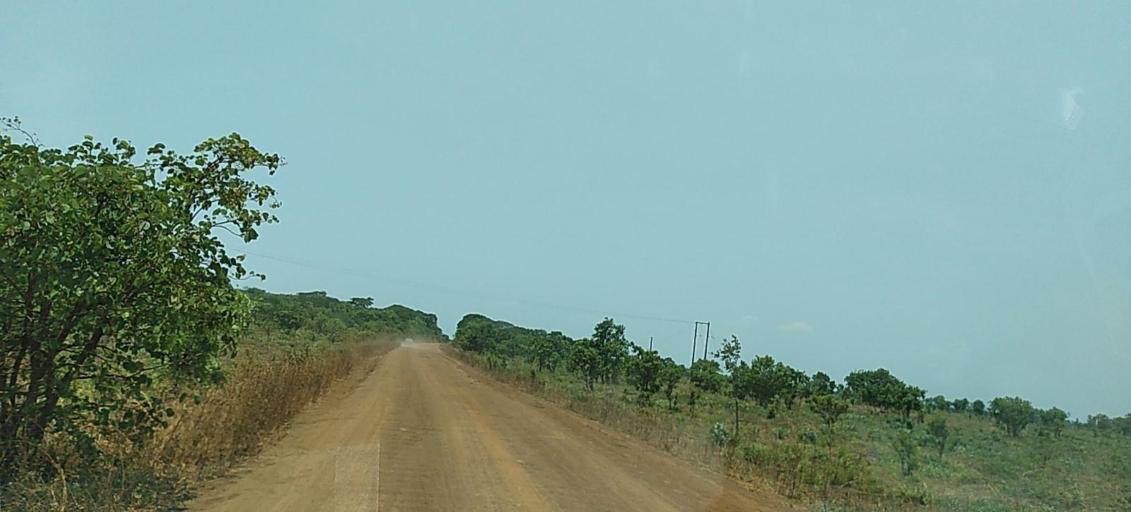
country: ZM
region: Copperbelt
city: Mpongwe
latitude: -13.6922
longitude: 27.8625
